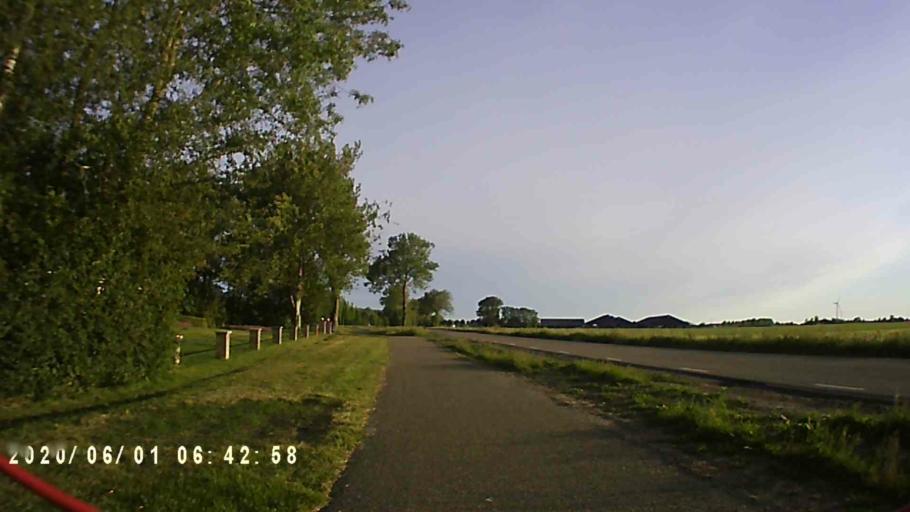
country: NL
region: Friesland
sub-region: Gemeente Kollumerland en Nieuwkruisland
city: Kollum
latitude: 53.2965
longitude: 6.1533
